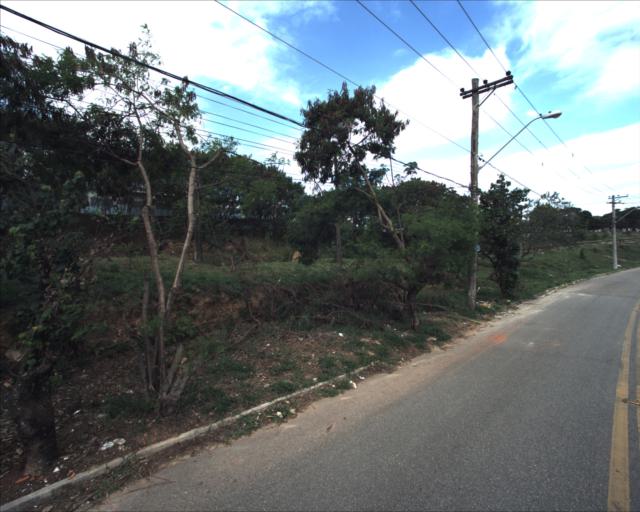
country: BR
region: Sao Paulo
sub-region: Sorocaba
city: Sorocaba
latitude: -23.4921
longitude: -47.4933
